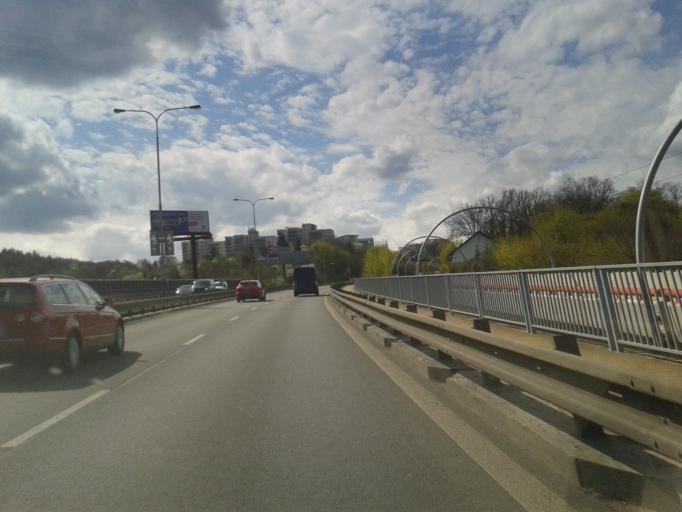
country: CZ
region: Praha
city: Branik
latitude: 50.0360
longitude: 14.3971
